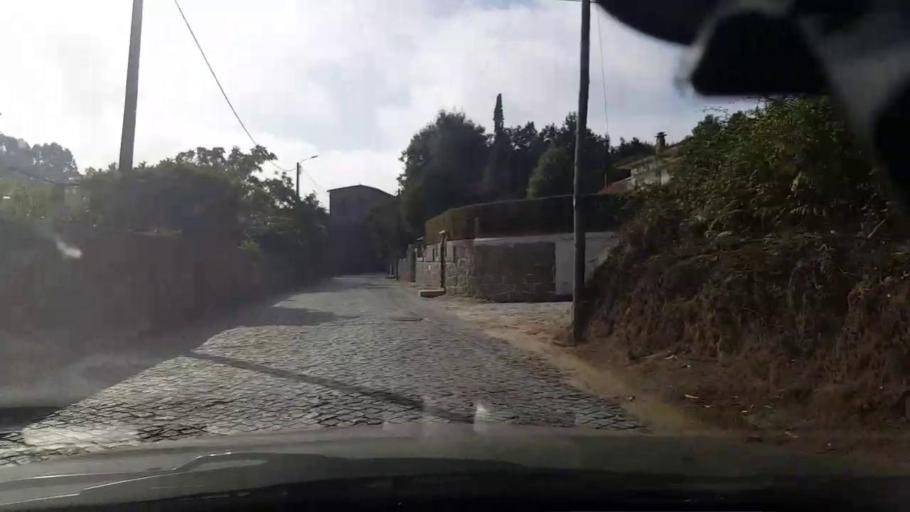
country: PT
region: Porto
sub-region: Maia
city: Gemunde
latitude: 41.2693
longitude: -8.6772
